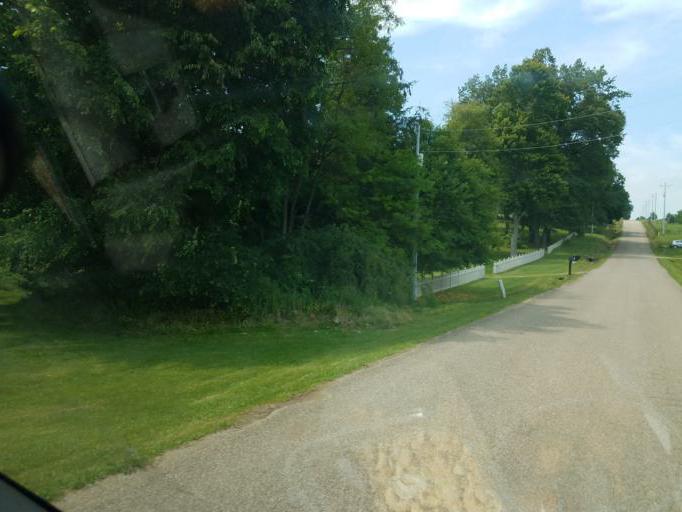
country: US
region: Ohio
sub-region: Knox County
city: Oak Hill
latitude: 40.2752
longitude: -82.2427
